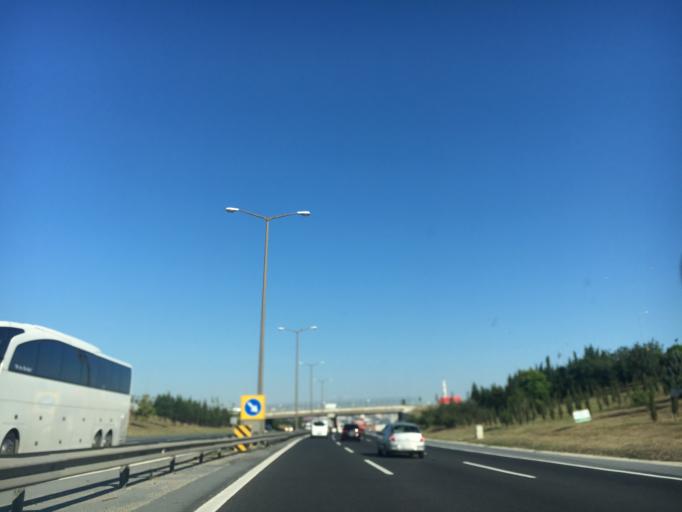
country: TR
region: Istanbul
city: Esenyurt
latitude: 41.0555
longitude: 28.6641
